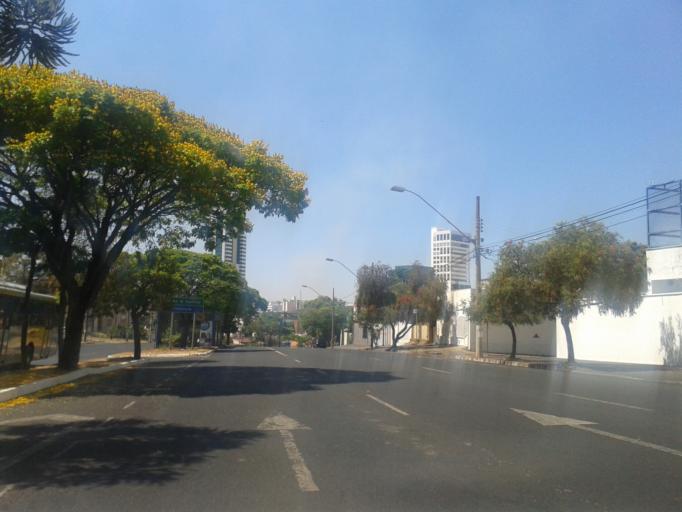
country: BR
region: Minas Gerais
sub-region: Uberlandia
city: Uberlandia
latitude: -18.9125
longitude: -48.2659
